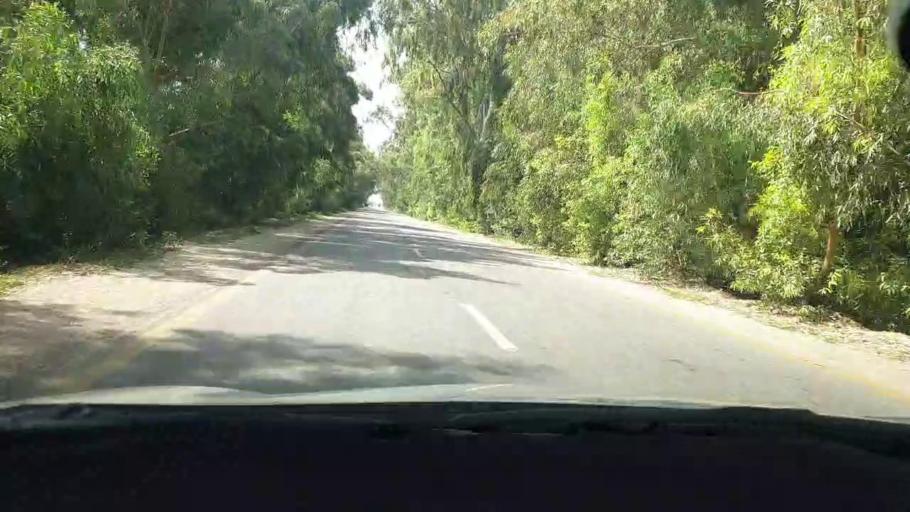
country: PK
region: Sindh
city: Mirpur Khas
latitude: 25.6563
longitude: 69.0999
